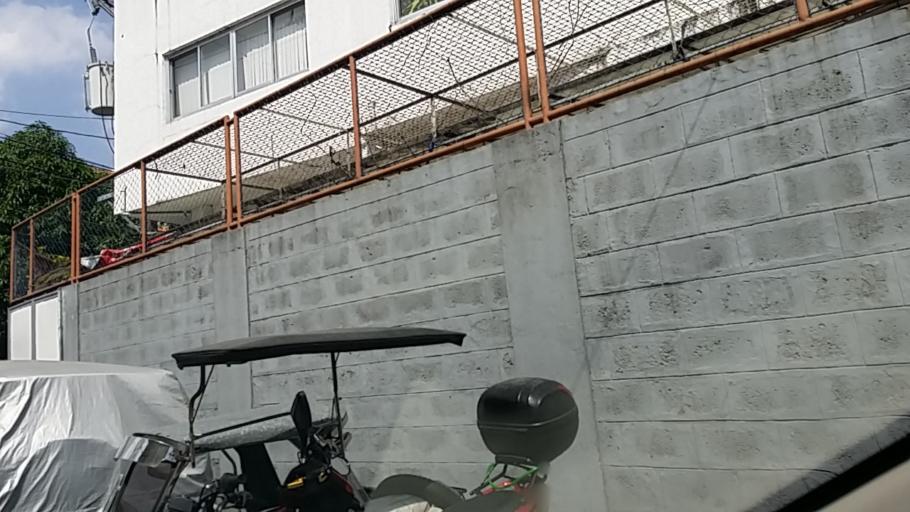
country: PH
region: Metro Manila
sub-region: Mandaluyong
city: Mandaluyong City
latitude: 14.5758
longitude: 121.0462
